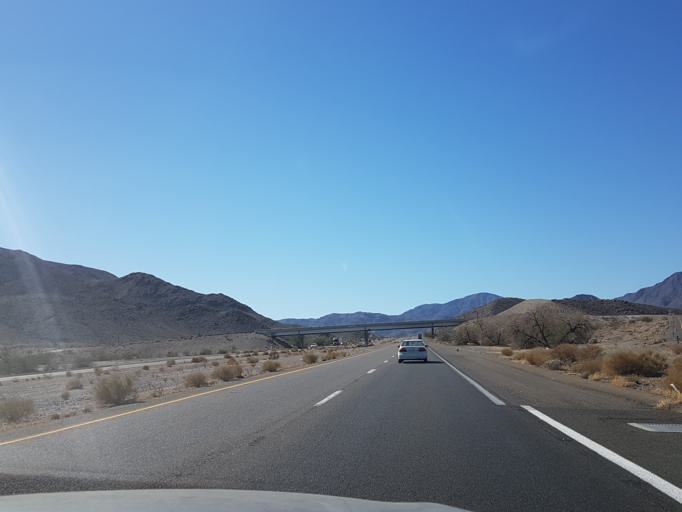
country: US
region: California
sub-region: San Bernardino County
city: Fort Irwin
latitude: 35.1962
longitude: -116.1380
